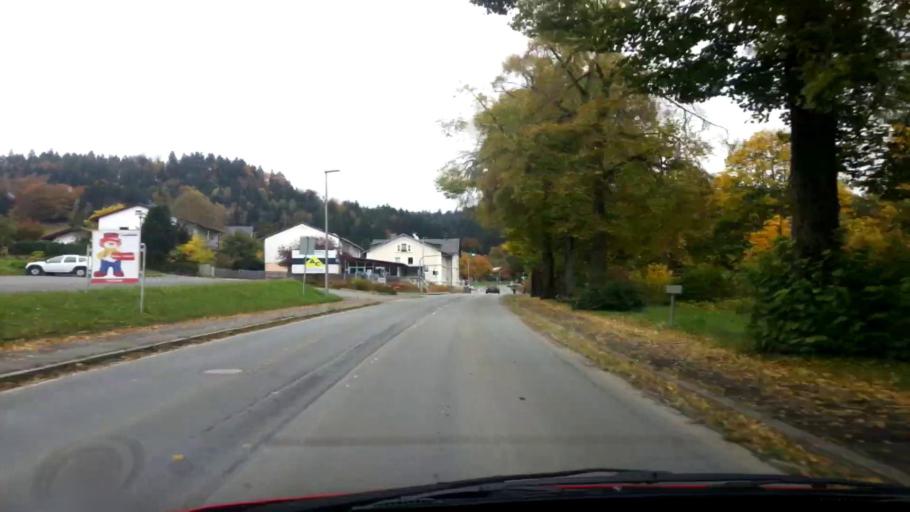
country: DE
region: Bavaria
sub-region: Upper Franconia
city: Warmensteinach
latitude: 49.9979
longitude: 11.7794
